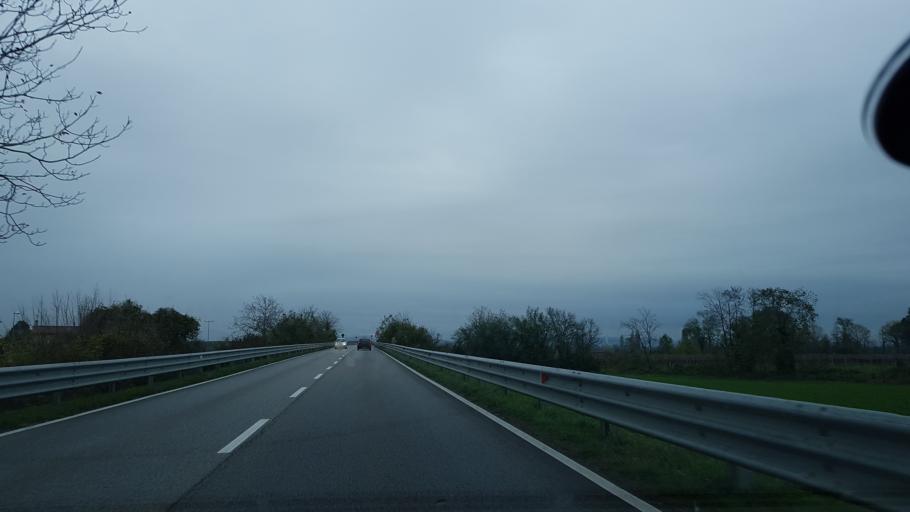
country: IT
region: Friuli Venezia Giulia
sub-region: Provincia di Gorizia
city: Begliano
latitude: 45.8146
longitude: 13.4601
